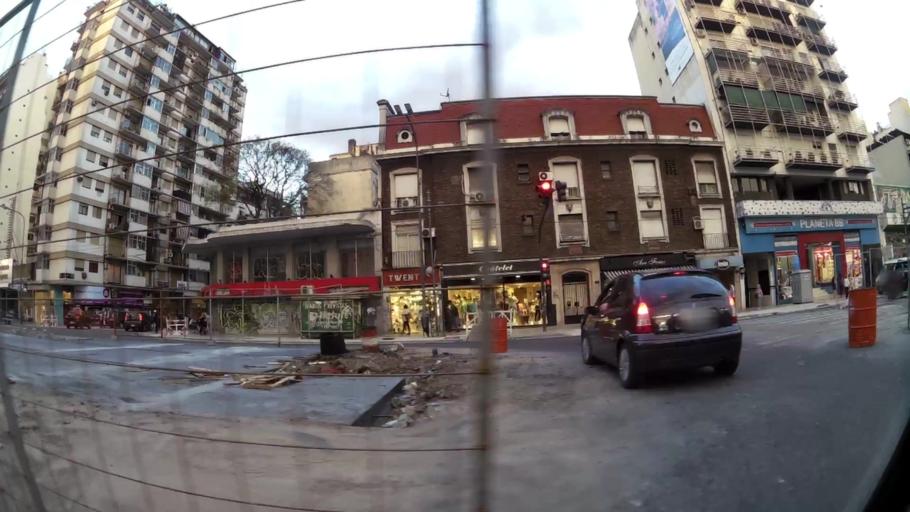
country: AR
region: Buenos Aires F.D.
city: Colegiales
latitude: -34.5576
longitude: -58.4606
